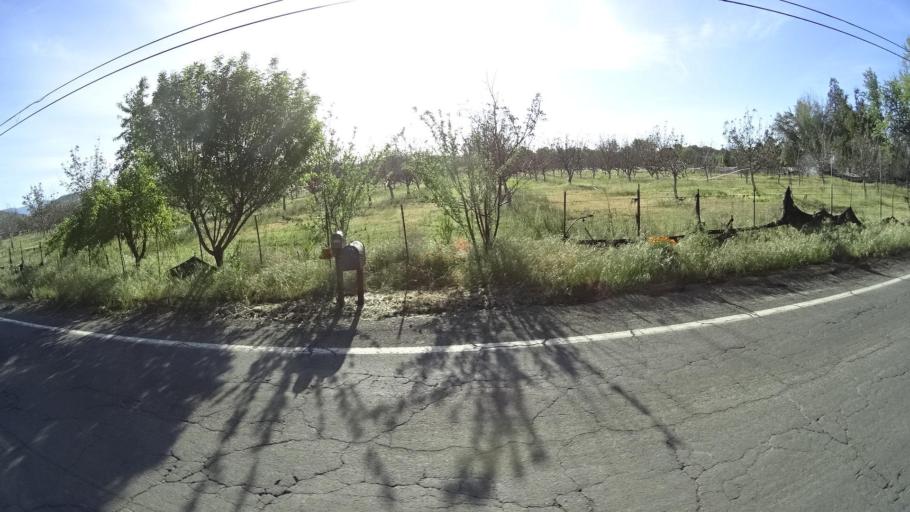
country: US
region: California
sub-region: Lake County
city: North Lakeport
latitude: 39.0757
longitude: -122.9498
